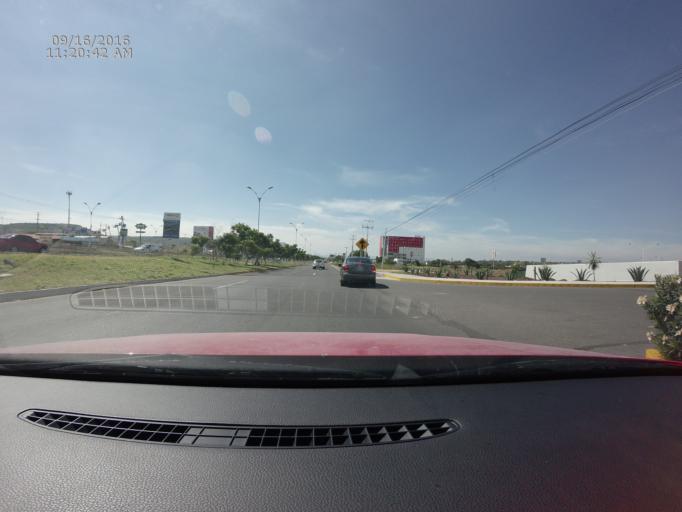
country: MX
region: Queretaro
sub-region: Queretaro
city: El Salitre
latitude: 20.6729
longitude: -100.4343
